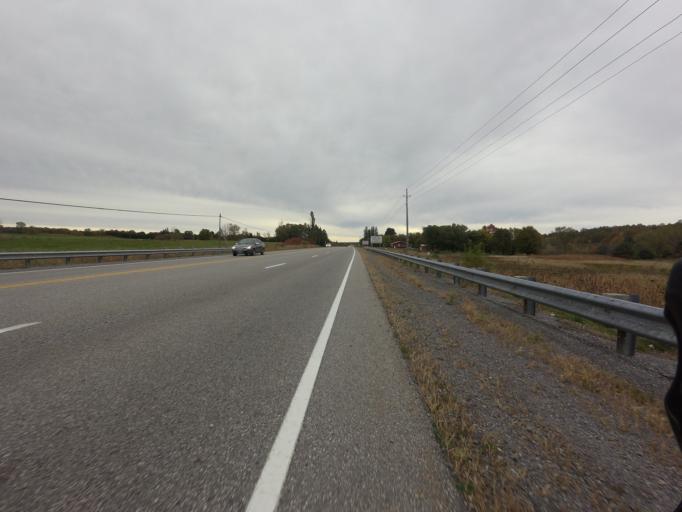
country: CA
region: Ontario
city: Gananoque
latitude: 44.4606
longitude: -76.2631
